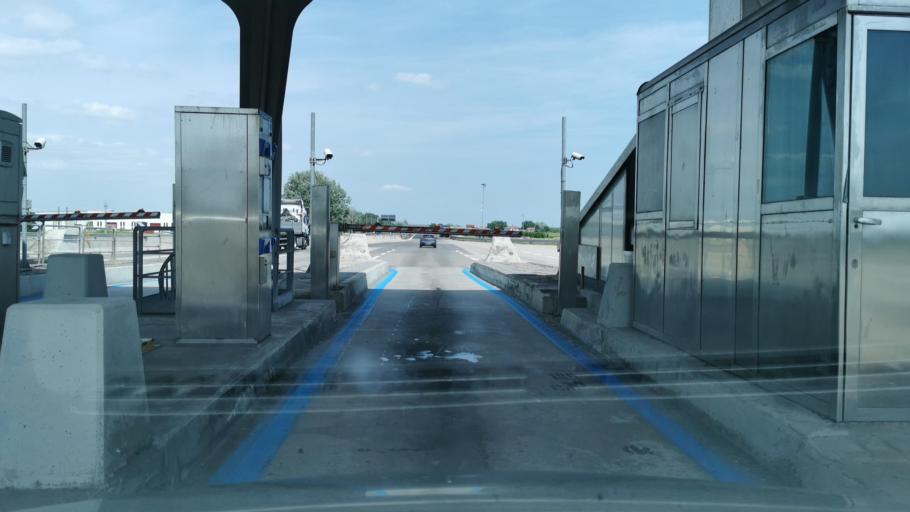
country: IT
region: Emilia-Romagna
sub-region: Provincia di Ravenna
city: Barbiano
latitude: 44.3871
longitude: 11.9085
